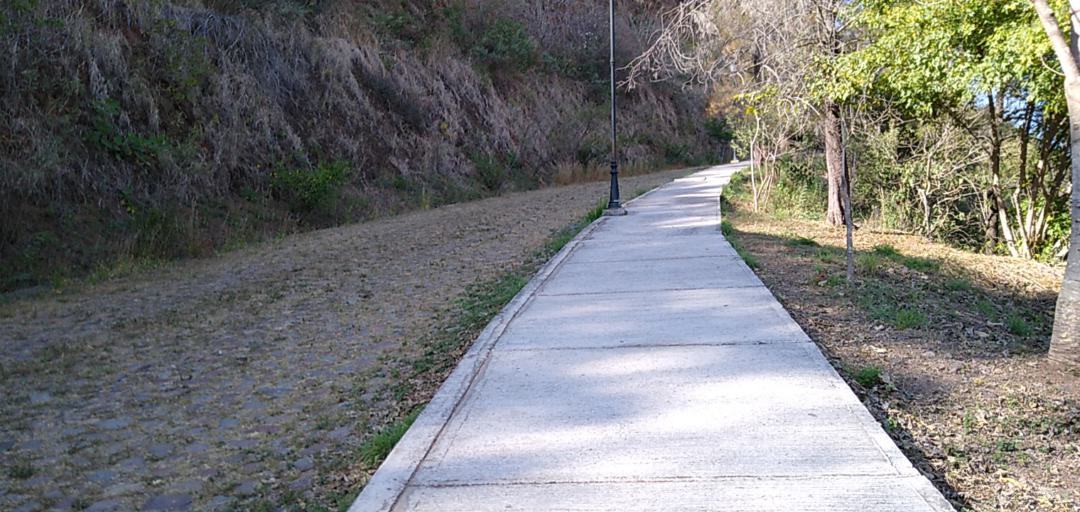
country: MX
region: Nayarit
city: Tepic
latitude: 21.5325
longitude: -104.8828
